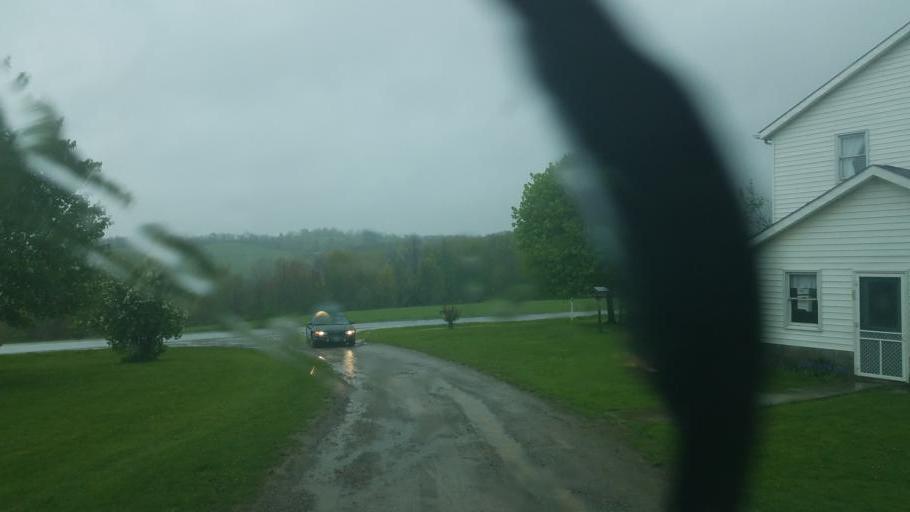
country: US
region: Pennsylvania
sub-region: Tioga County
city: Elkland
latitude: 42.0812
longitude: -77.4330
